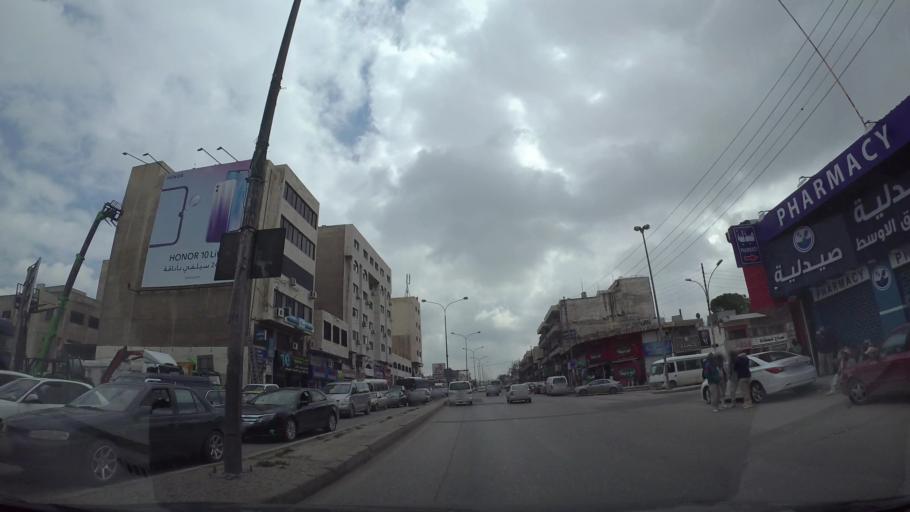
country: JO
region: Amman
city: Al Quwaysimah
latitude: 31.9202
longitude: 35.9383
